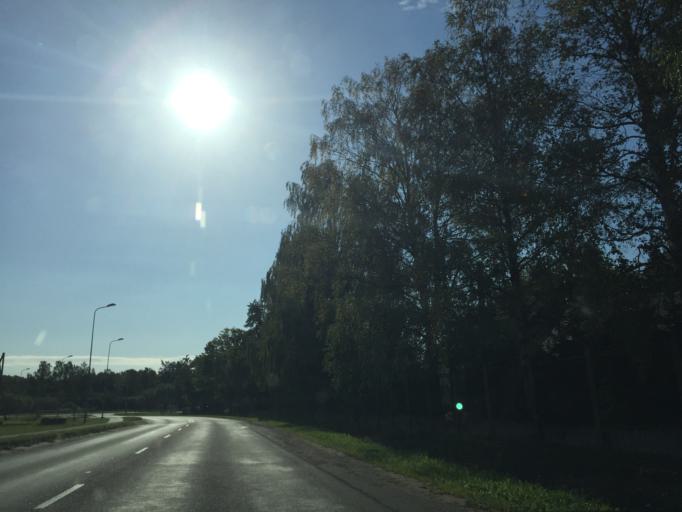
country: LV
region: Limbazu Rajons
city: Limbazi
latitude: 57.5104
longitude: 24.6954
